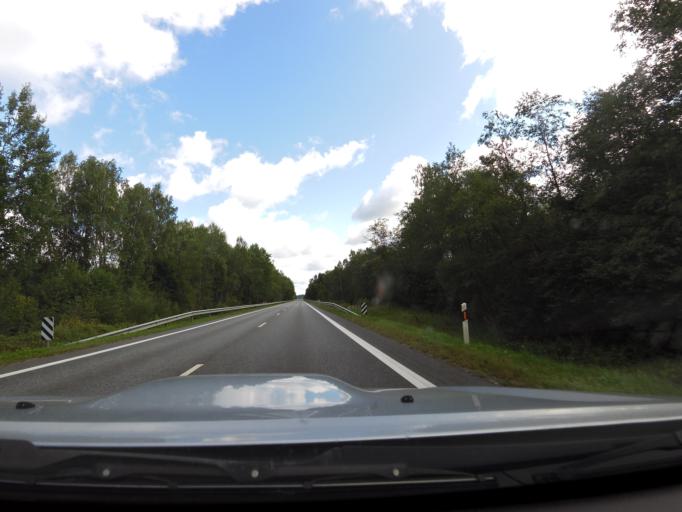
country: LT
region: Utenos apskritis
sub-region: Utena
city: Utena
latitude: 55.5698
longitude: 25.7766
